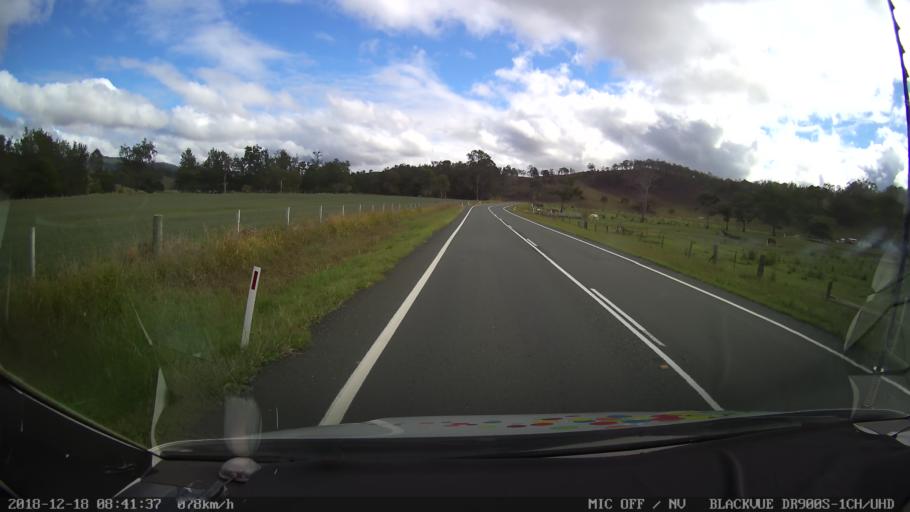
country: AU
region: Queensland
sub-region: Logan
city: Cedar Vale
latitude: -28.2345
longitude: 152.8584
